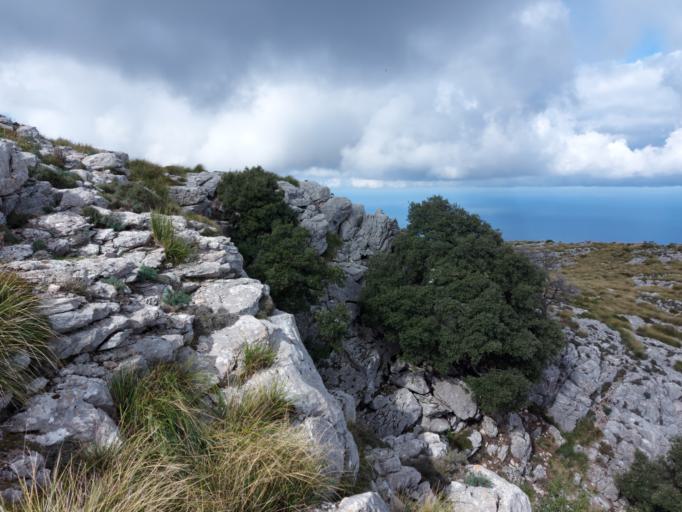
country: ES
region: Balearic Islands
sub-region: Illes Balears
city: Escorca
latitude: 39.8186
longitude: 2.8450
